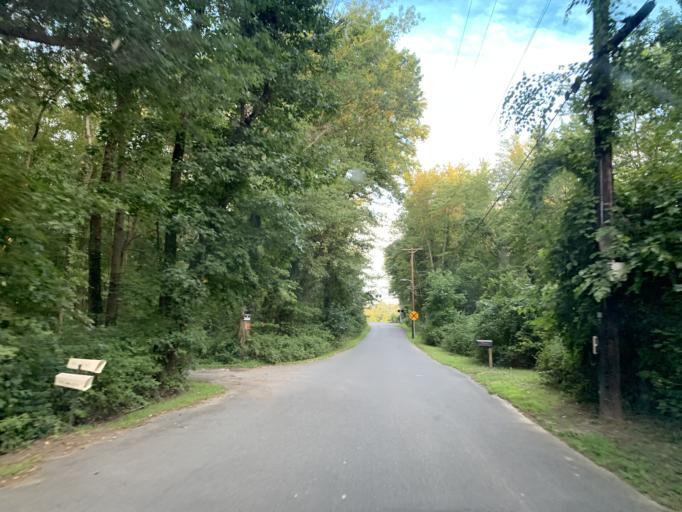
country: US
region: Maryland
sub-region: Harford County
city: Aberdeen
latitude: 39.5195
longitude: -76.1550
